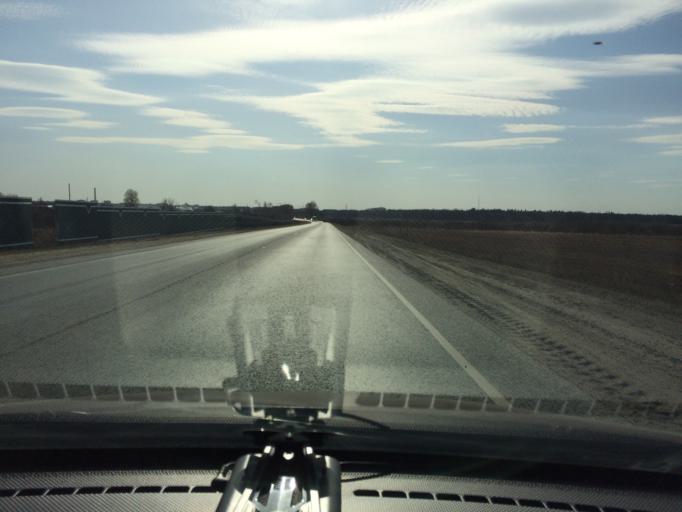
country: RU
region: Mariy-El
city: Yoshkar-Ola
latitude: 56.6570
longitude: 47.9638
